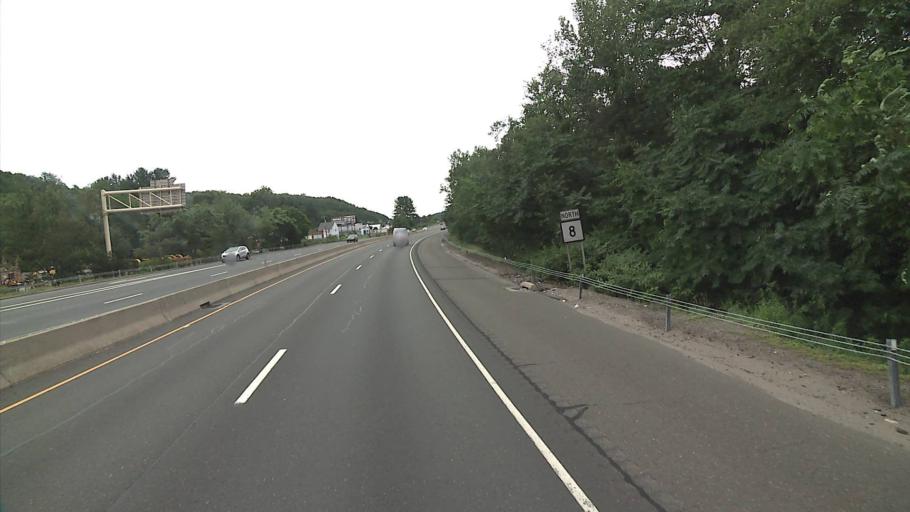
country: US
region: Connecticut
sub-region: New Haven County
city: Ansonia
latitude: 41.3633
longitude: -73.0920
